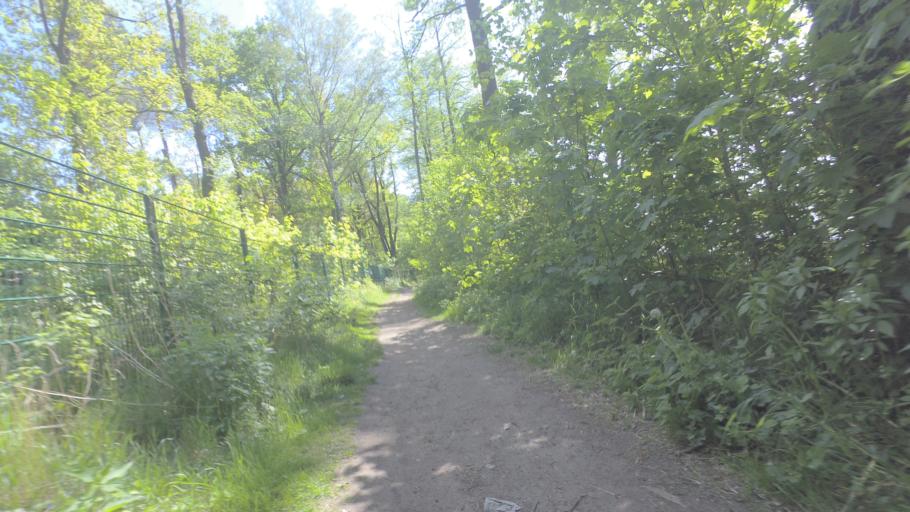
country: DE
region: Brandenburg
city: Woltersdorf
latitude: 52.4334
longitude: 13.7685
